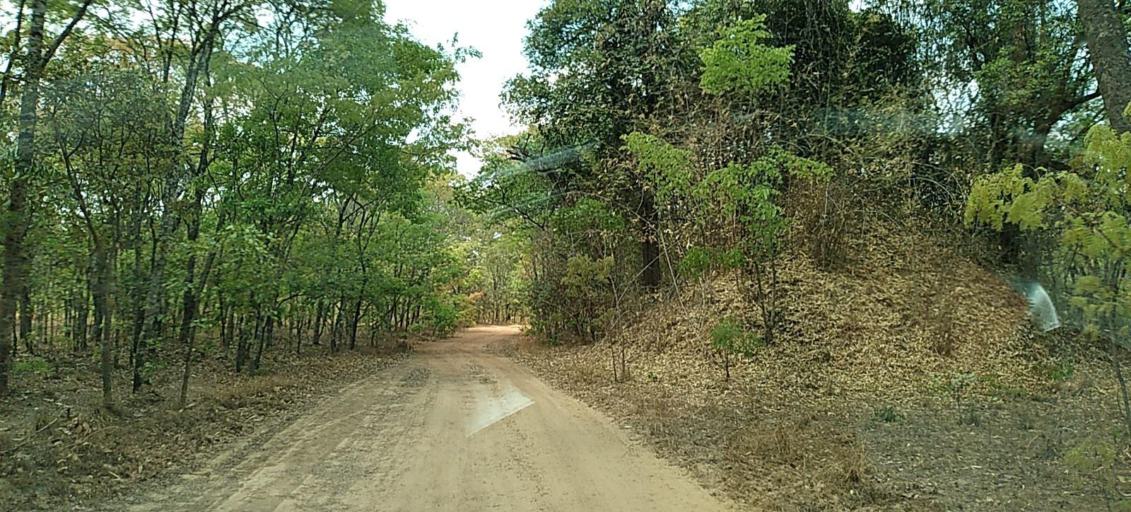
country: ZM
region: Copperbelt
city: Chililabombwe
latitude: -12.5016
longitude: 27.6384
